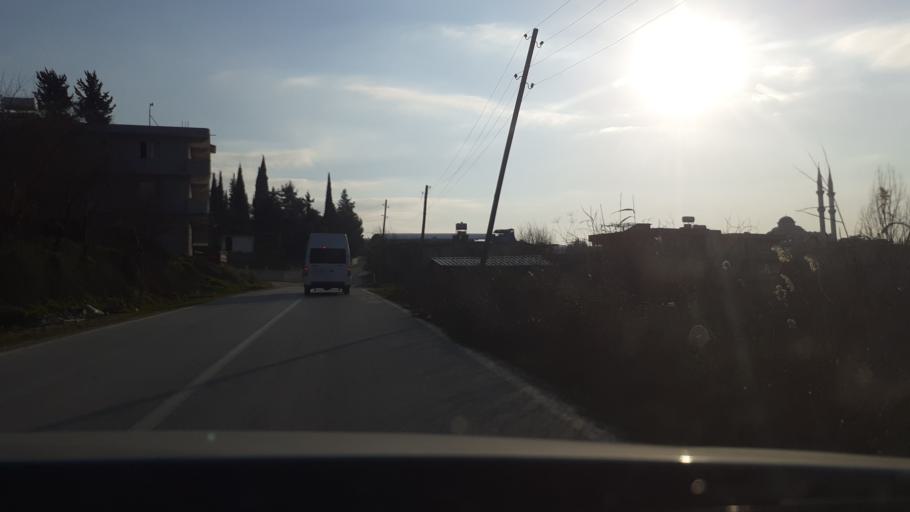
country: TR
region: Hatay
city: Oymakli
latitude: 36.1139
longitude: 36.3014
